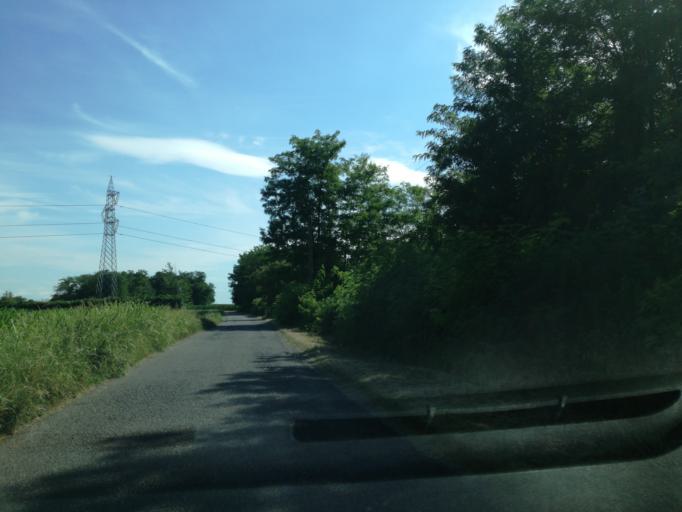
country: IT
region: Lombardy
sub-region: Provincia di Lecco
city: Verderio Inferiore
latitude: 45.6610
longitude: 9.4250
